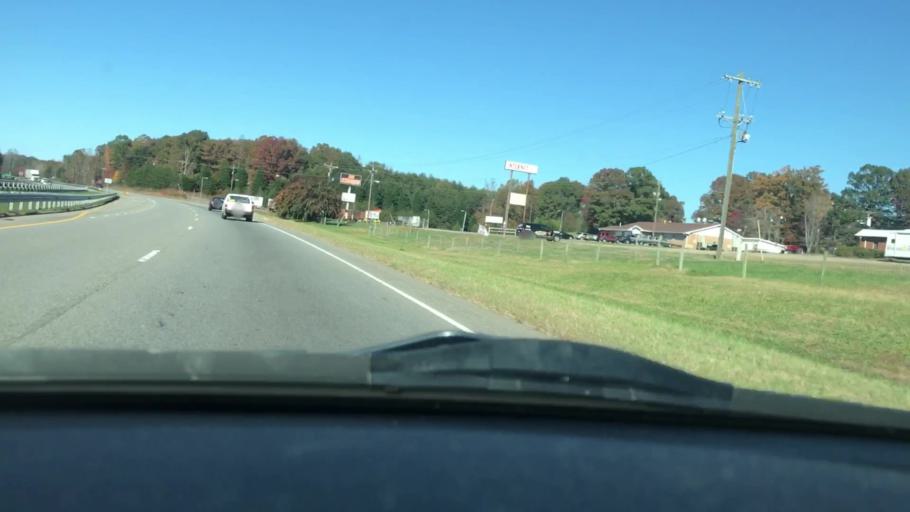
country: US
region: North Carolina
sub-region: Rockingham County
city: Stoneville
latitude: 36.4781
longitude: -79.9242
